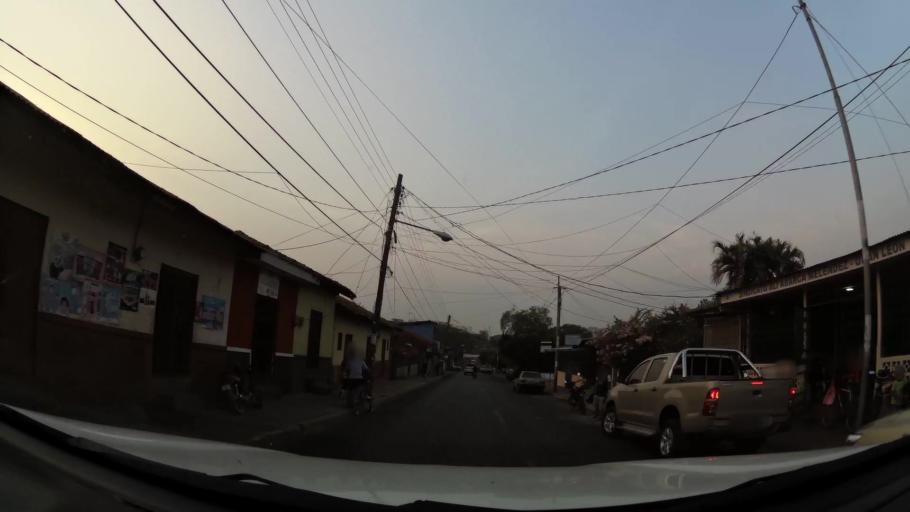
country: NI
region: Leon
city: Leon
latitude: 12.4298
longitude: -86.8769
